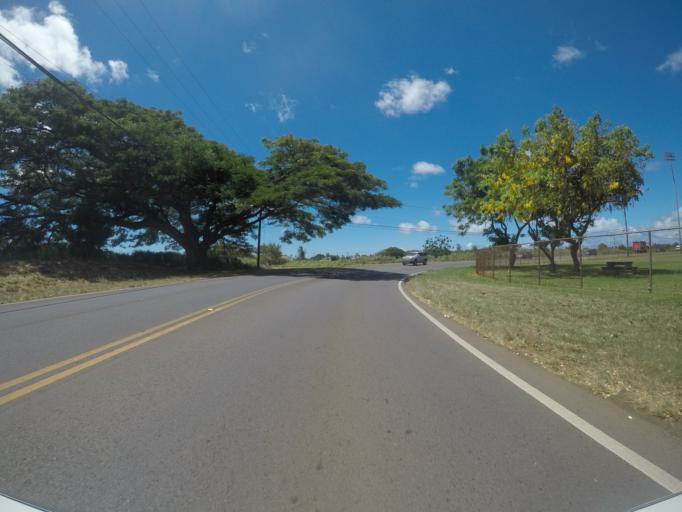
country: US
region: Hawaii
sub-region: Honolulu County
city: Waialua
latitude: 21.5762
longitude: -158.1241
